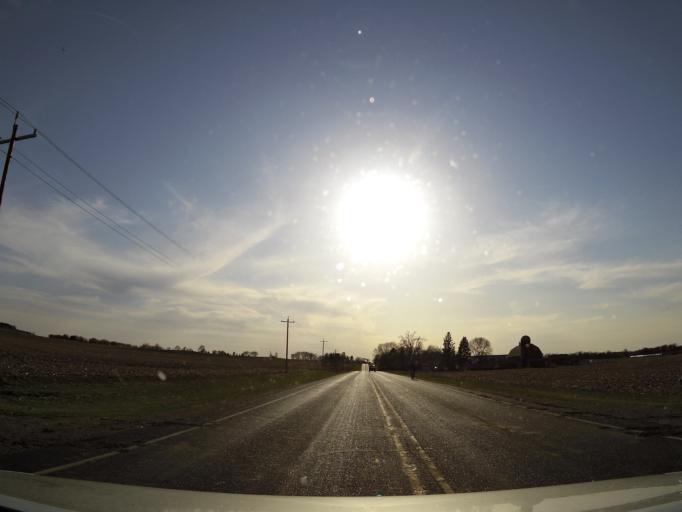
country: US
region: Wisconsin
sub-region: Pierce County
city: River Falls
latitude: 44.8249
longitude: -92.7020
